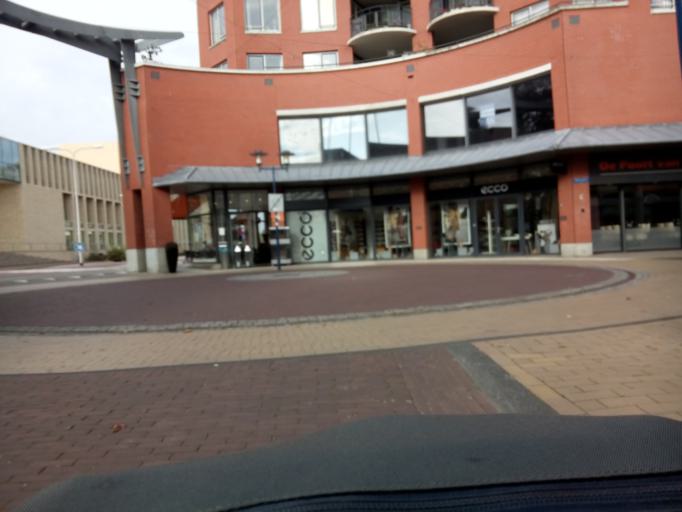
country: NL
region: Drenthe
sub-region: Gemeente Assen
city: Assen
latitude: 52.9944
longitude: 6.5602
